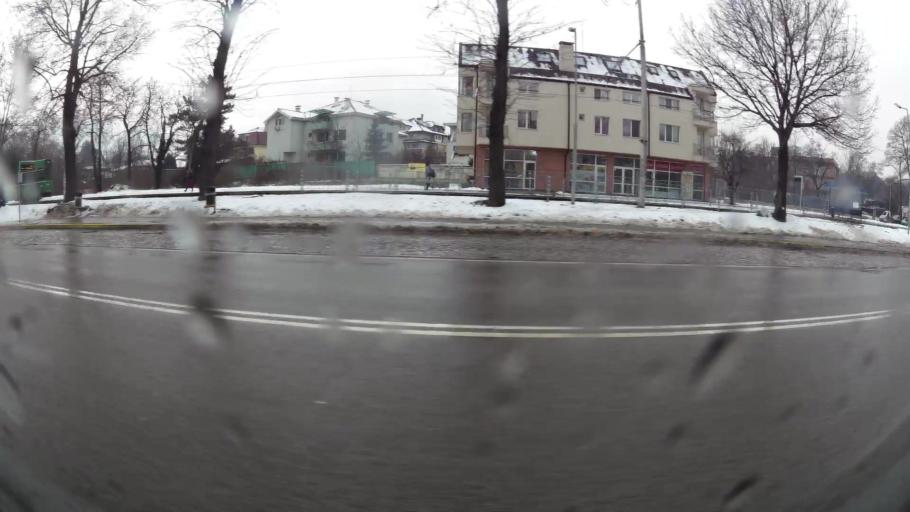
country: BG
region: Sofia-Capital
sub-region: Stolichna Obshtina
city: Sofia
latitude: 42.6765
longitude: 23.2683
